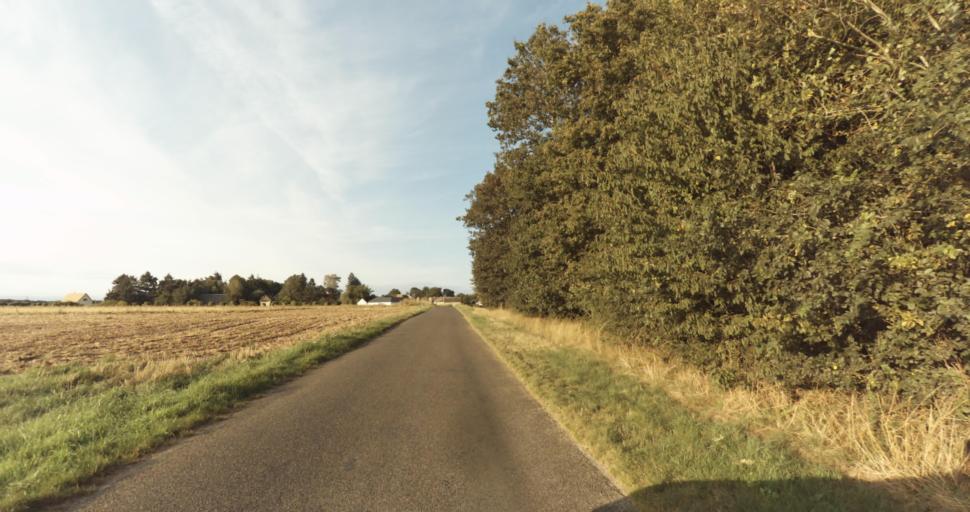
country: FR
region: Haute-Normandie
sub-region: Departement de l'Eure
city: Marcilly-sur-Eure
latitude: 48.8351
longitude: 1.2793
